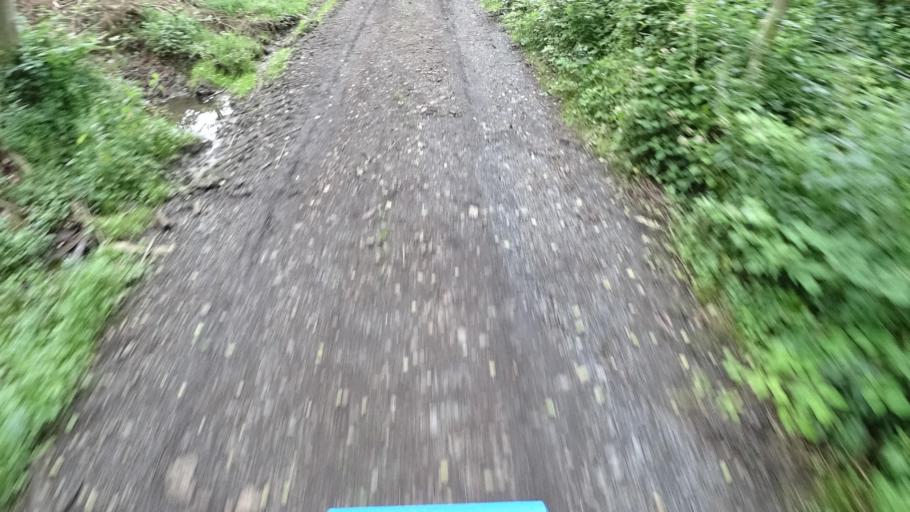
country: DE
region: Rheinland-Pfalz
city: Vettelschoss
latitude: 50.6110
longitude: 7.3280
